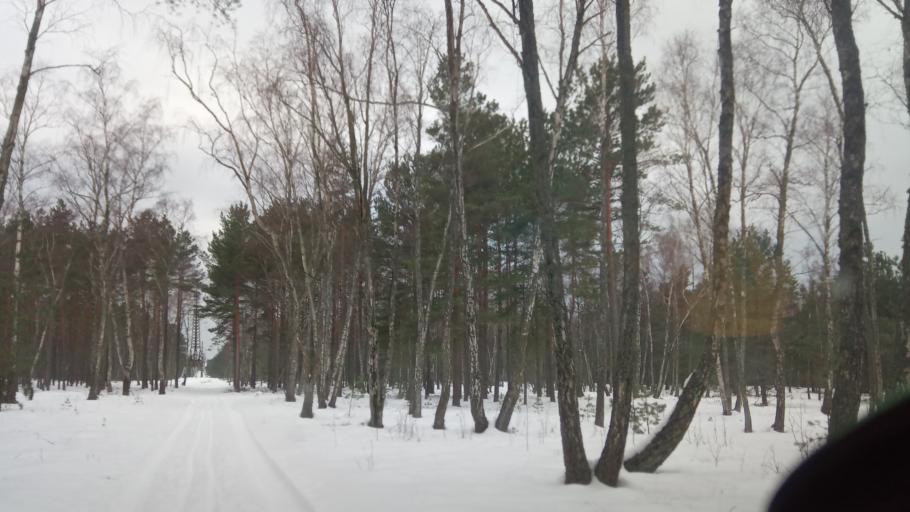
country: LT
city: Neringa
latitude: 55.4184
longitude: 21.0986
